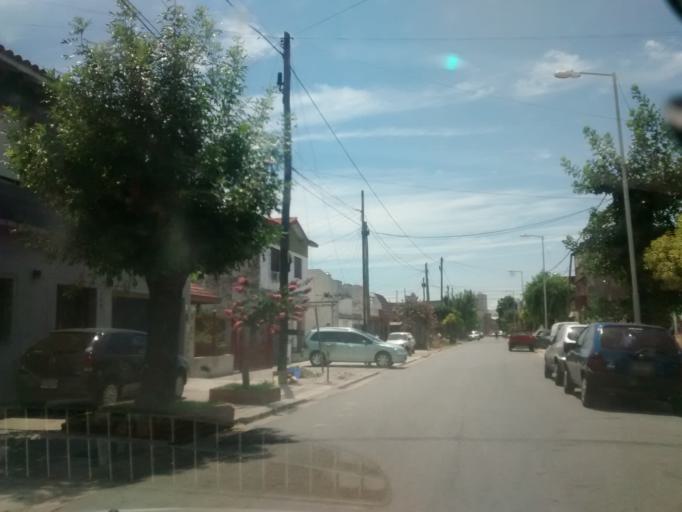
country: AR
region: Buenos Aires
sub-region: Partido de Avellaneda
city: Avellaneda
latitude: -34.6792
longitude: -58.3564
